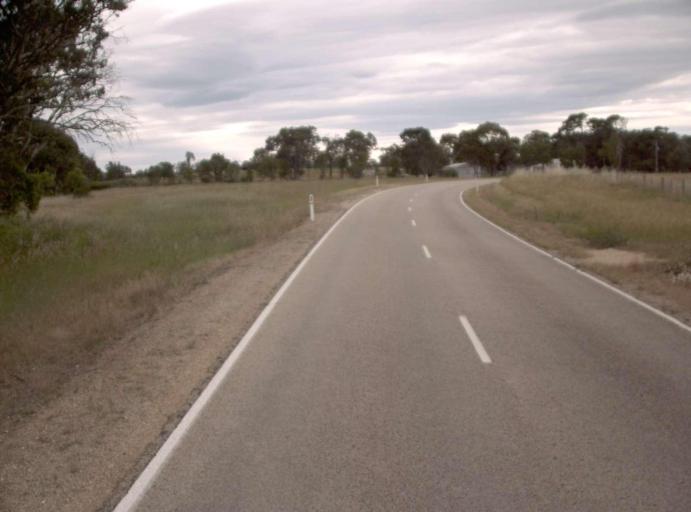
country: AU
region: Victoria
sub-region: East Gippsland
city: Bairnsdale
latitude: -37.9750
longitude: 147.4652
